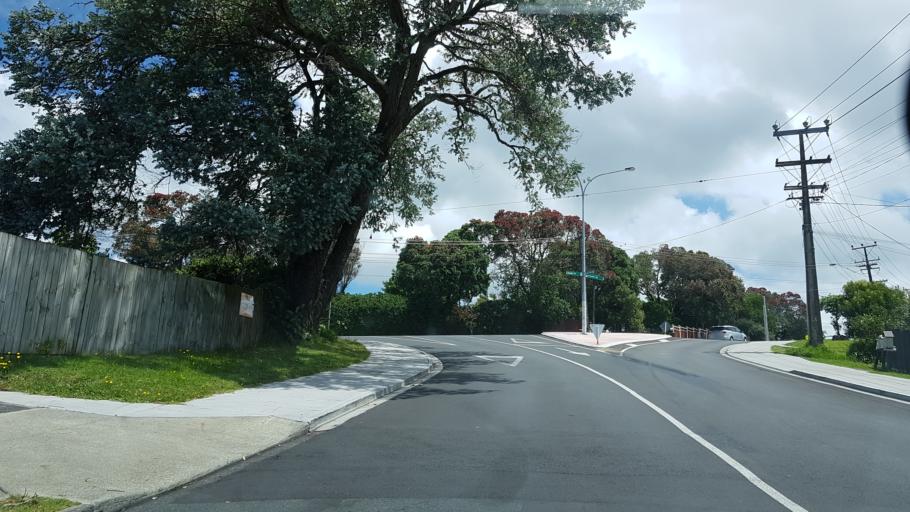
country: NZ
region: Auckland
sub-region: Auckland
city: North Shore
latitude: -36.8007
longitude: 174.7369
